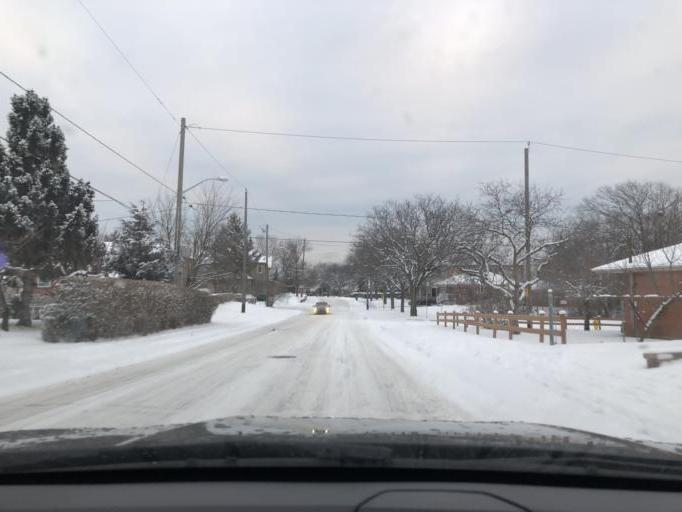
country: CA
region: Ontario
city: Toronto
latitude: 43.7040
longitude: -79.4818
